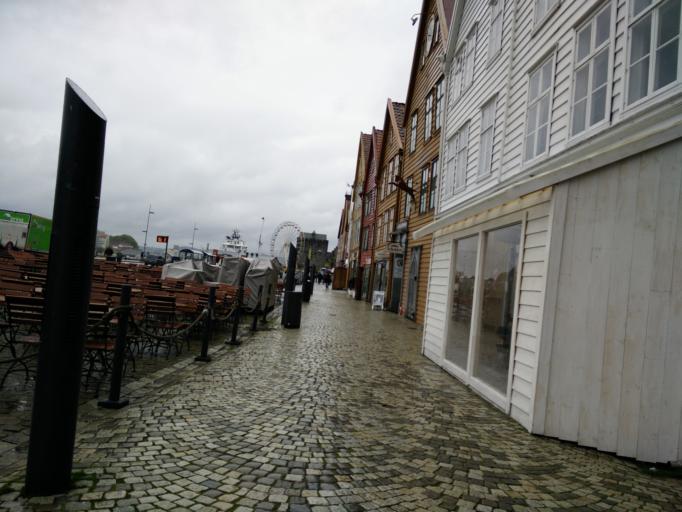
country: NO
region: Hordaland
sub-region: Bergen
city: Bergen
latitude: 60.3970
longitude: 5.3237
